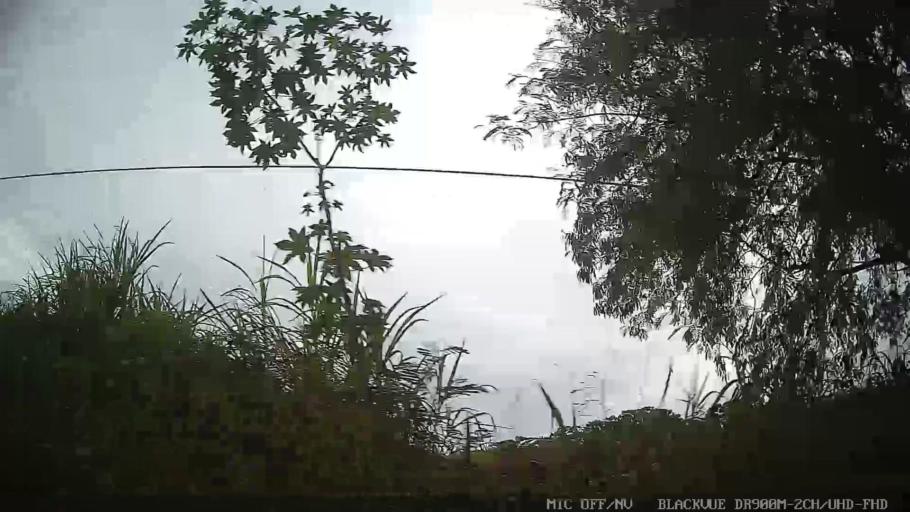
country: BR
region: Sao Paulo
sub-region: Jaguariuna
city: Jaguariuna
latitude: -22.7715
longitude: -47.0158
